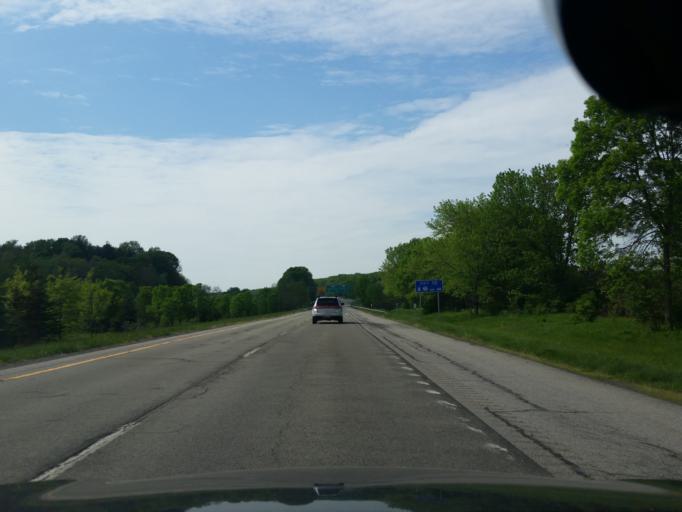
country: US
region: New York
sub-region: Chautauqua County
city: Lakewood
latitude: 42.1626
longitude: -79.3809
